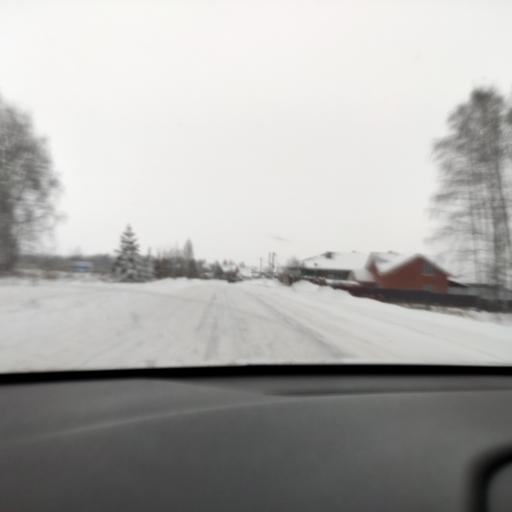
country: RU
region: Tatarstan
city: Vysokaya Gora
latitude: 55.9654
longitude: 49.1708
